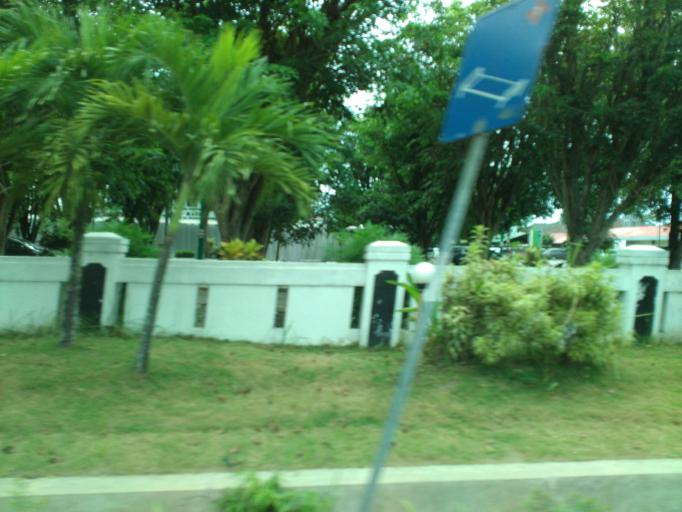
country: ID
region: Central Java
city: Klaten
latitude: -7.6866
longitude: 110.6348
